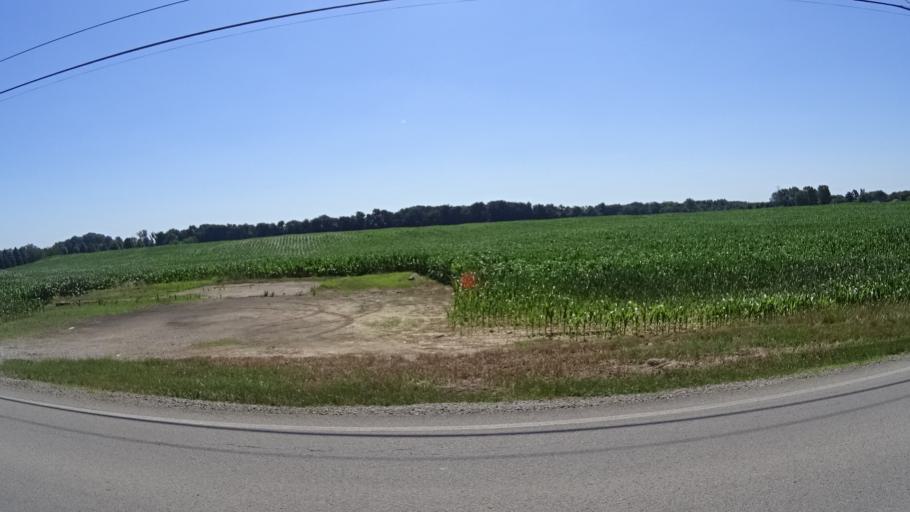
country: US
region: Ohio
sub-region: Erie County
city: Huron
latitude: 41.3635
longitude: -82.5727
